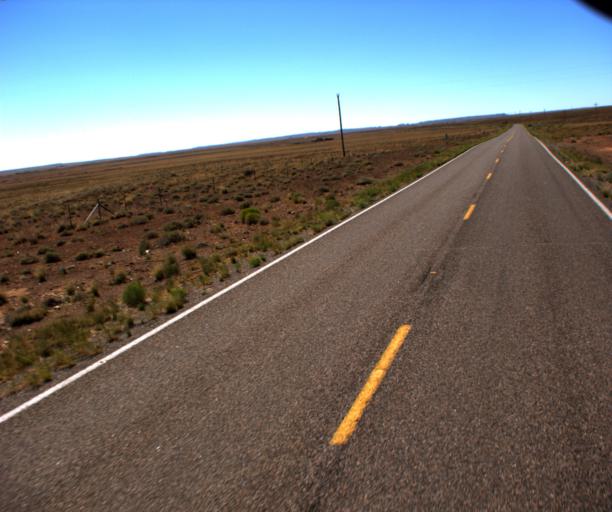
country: US
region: Arizona
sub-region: Coconino County
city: LeChee
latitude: 35.1814
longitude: -110.9299
